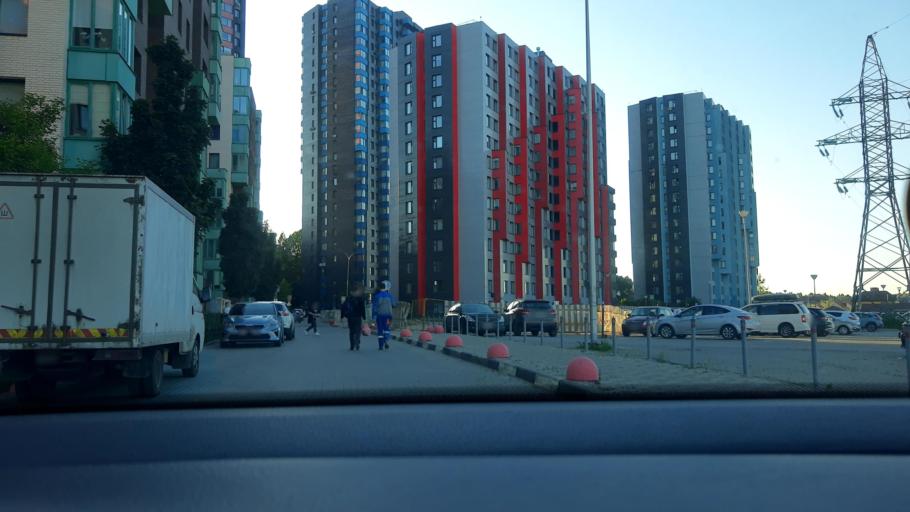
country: RU
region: Moskovskaya
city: Firsanovka
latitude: 55.9427
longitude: 37.2633
